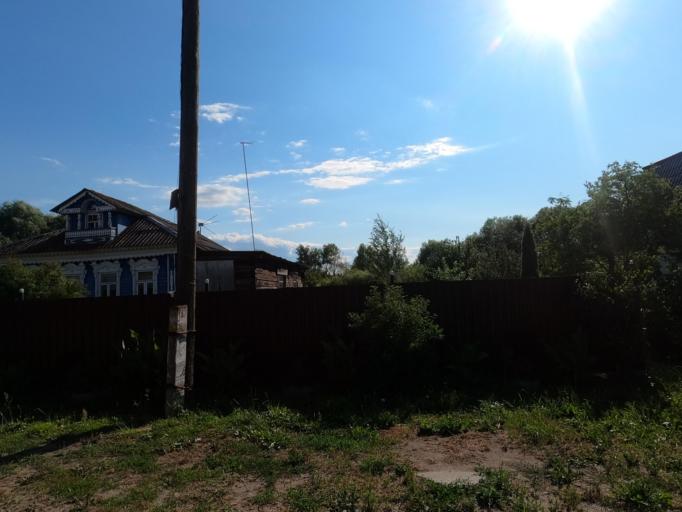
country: RU
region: Moskovskaya
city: Konobeyevo
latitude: 55.4081
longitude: 38.7017
